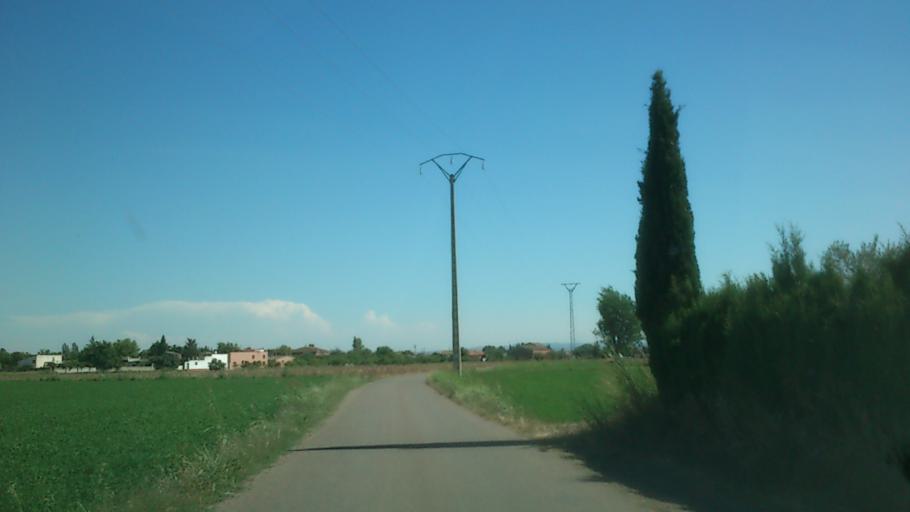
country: ES
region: Aragon
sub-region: Provincia de Zaragoza
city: Villanueva de Gallego
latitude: 41.7036
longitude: -0.8115
